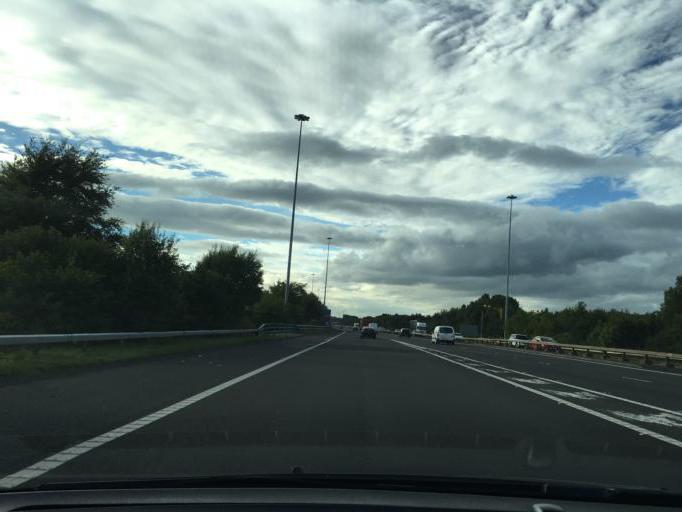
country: GB
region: Scotland
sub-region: South Lanarkshire
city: Hamilton
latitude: 55.7817
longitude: -4.0234
